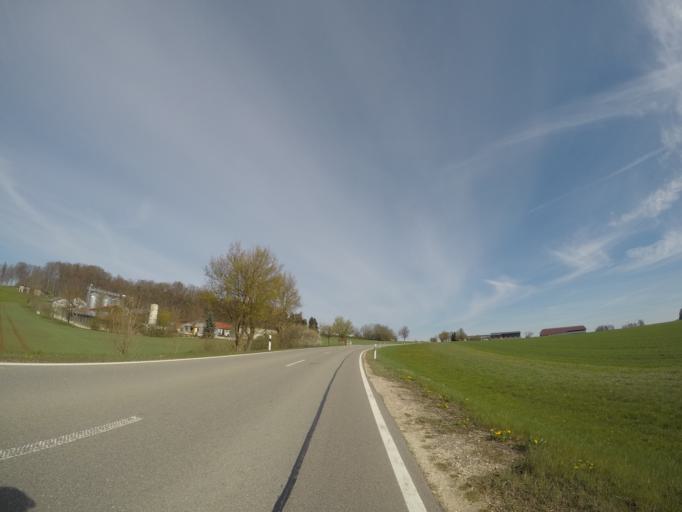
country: DE
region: Baden-Wuerttemberg
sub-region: Tuebingen Region
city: Laichingen
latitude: 48.5063
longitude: 9.6734
